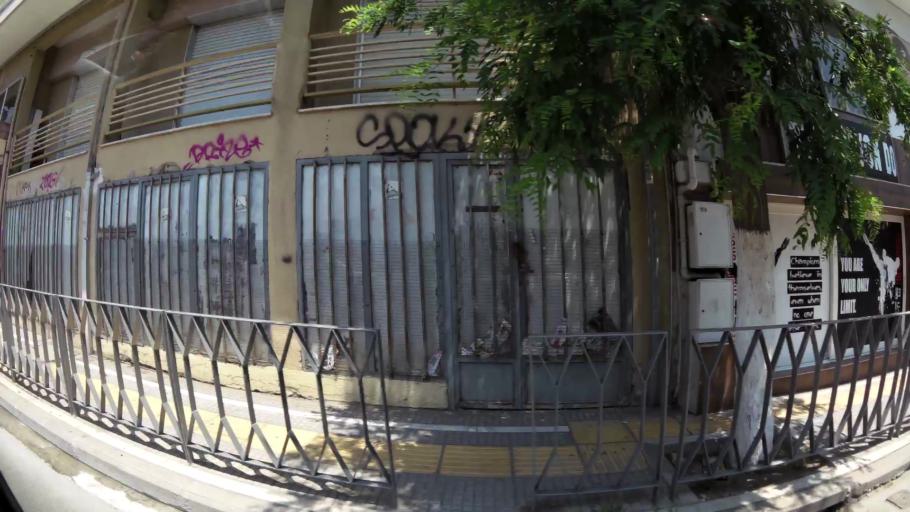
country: GR
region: Central Macedonia
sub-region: Nomos Thessalonikis
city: Ampelokipoi
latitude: 40.6502
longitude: 22.9205
